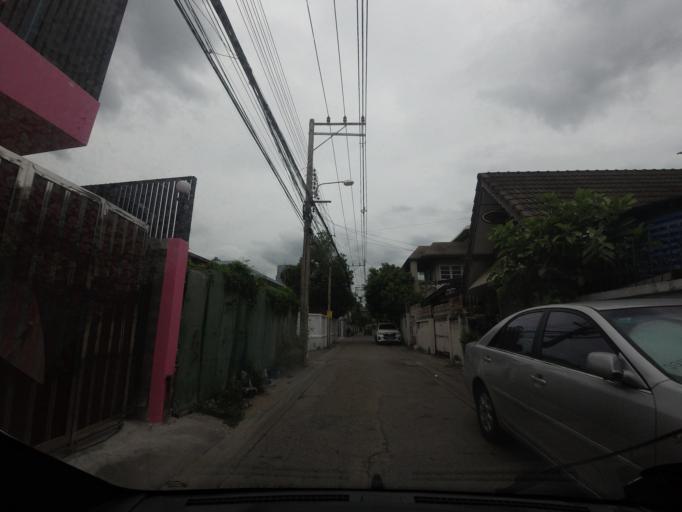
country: TH
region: Bangkok
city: Phaya Thai
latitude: 13.7904
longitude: 100.5402
